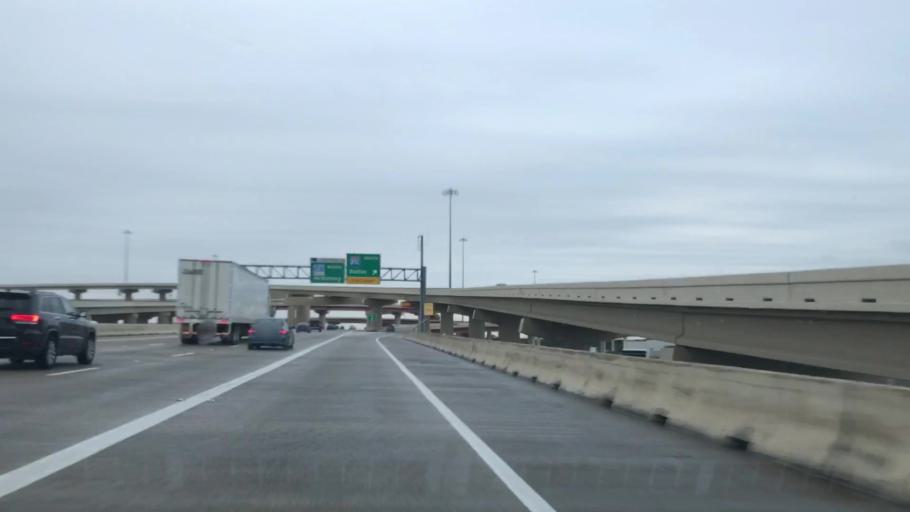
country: US
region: Texas
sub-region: Denton County
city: Lewisville
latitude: 32.9967
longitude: -96.9629
